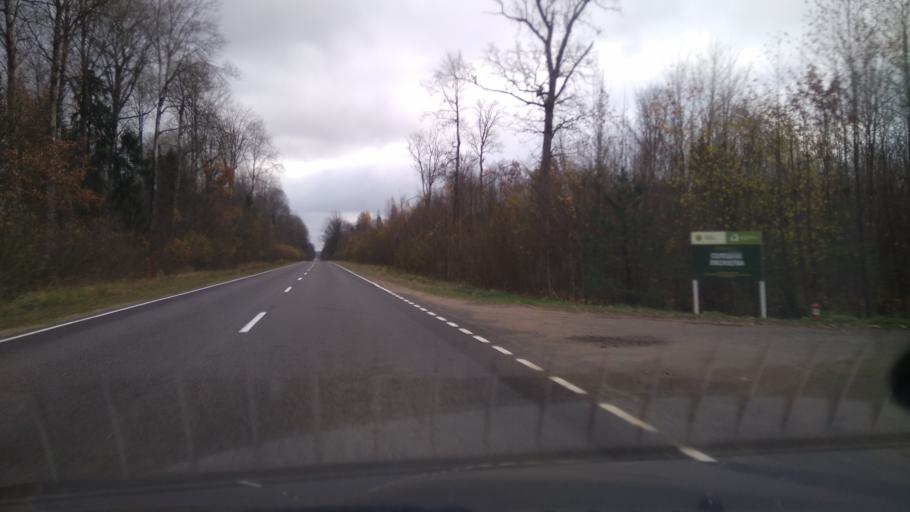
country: BY
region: Minsk
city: Urechcha
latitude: 53.2115
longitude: 27.8864
